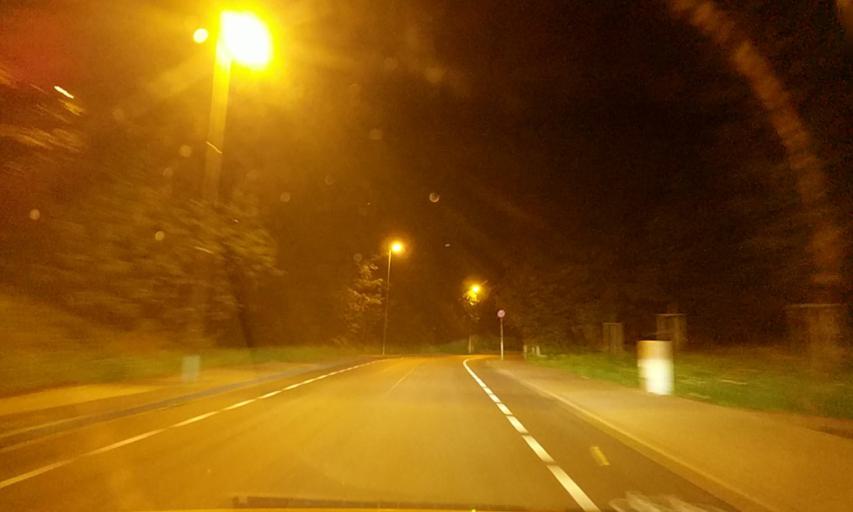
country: DE
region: Rheinland-Pfalz
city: Kaiserslautern
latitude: 49.4374
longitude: 7.7819
